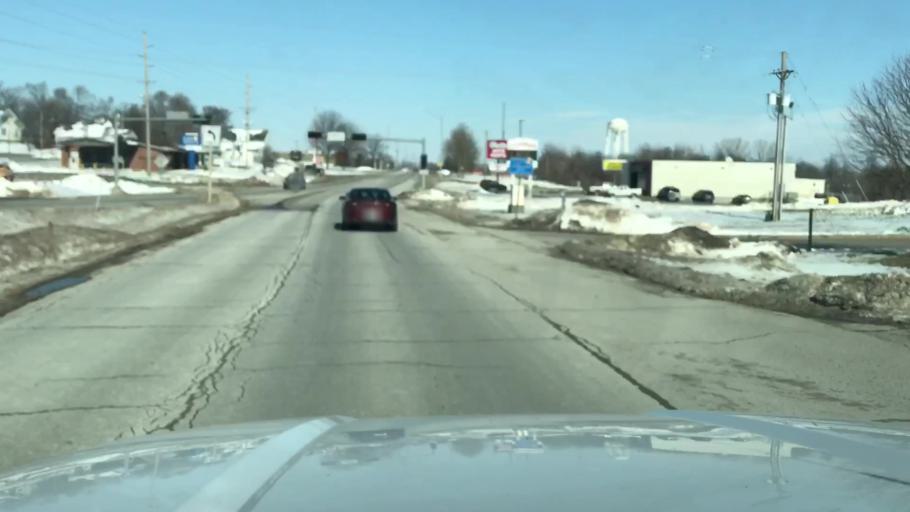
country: US
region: Missouri
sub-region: Andrew County
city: Savannah
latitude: 39.9400
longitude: -94.8218
